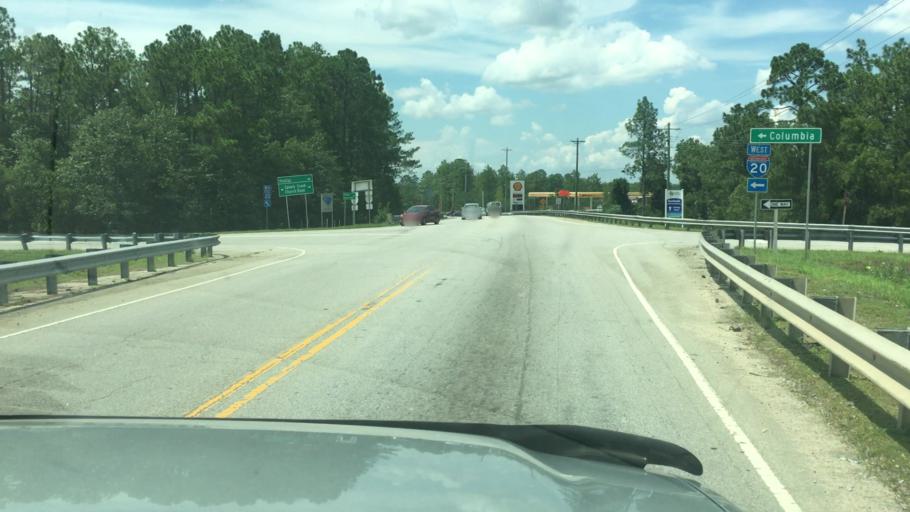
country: US
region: South Carolina
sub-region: Kershaw County
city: Elgin
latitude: 34.1052
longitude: -80.8296
